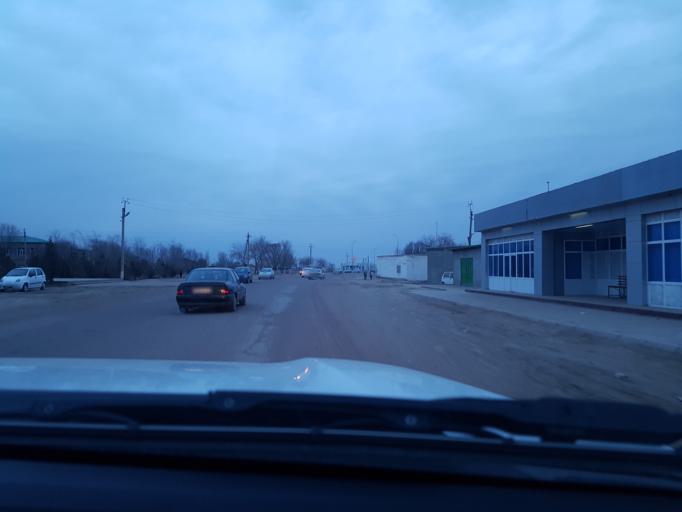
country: TM
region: Dasoguz
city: Yylanly
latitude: 41.8811
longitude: 59.6266
